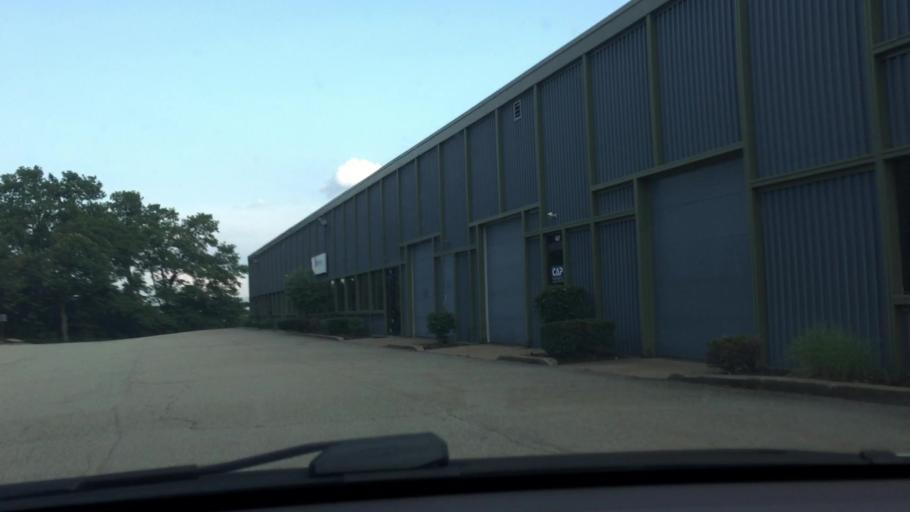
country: US
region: Pennsylvania
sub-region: Allegheny County
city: Rennerdale
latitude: 40.4339
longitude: -80.1323
